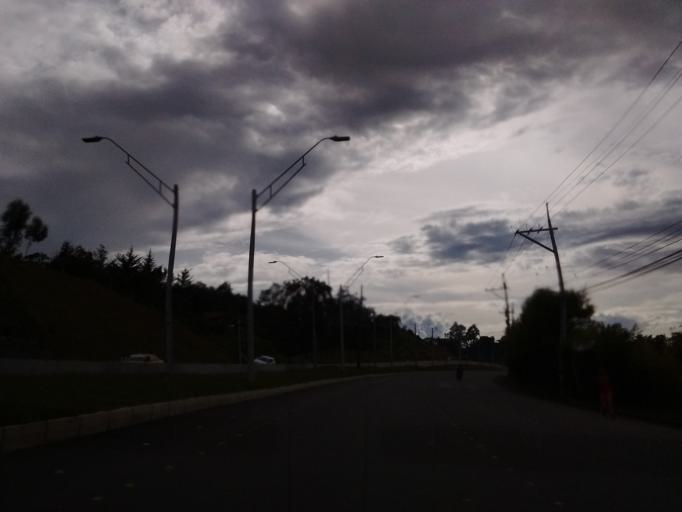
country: CO
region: Antioquia
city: Santuario
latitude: 6.1338
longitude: -75.2900
